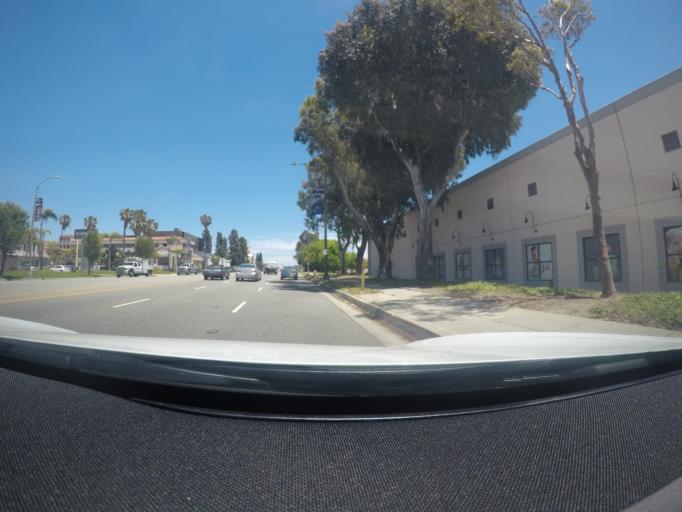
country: US
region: California
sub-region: Los Angeles County
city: Torrance
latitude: 33.8375
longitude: -118.3524
